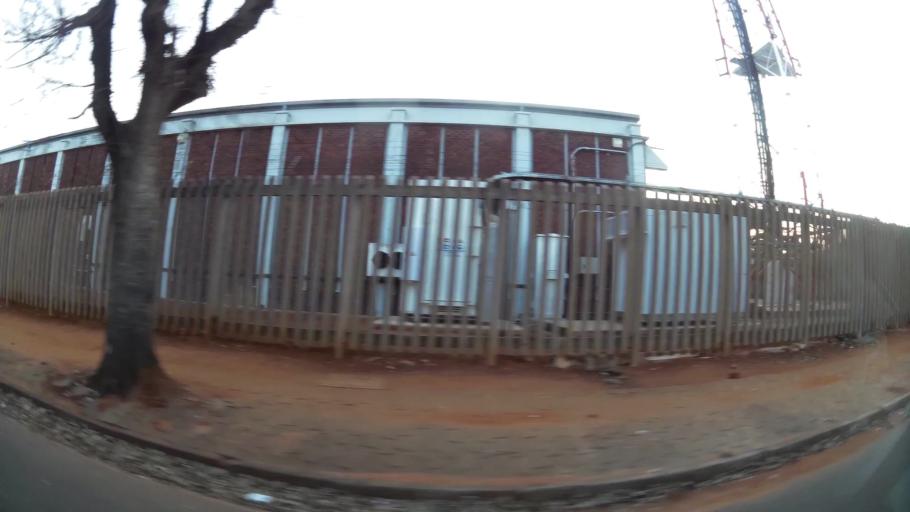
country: ZA
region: Gauteng
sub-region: Ekurhuleni Metropolitan Municipality
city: Tembisa
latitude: -26.0631
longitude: 28.2304
